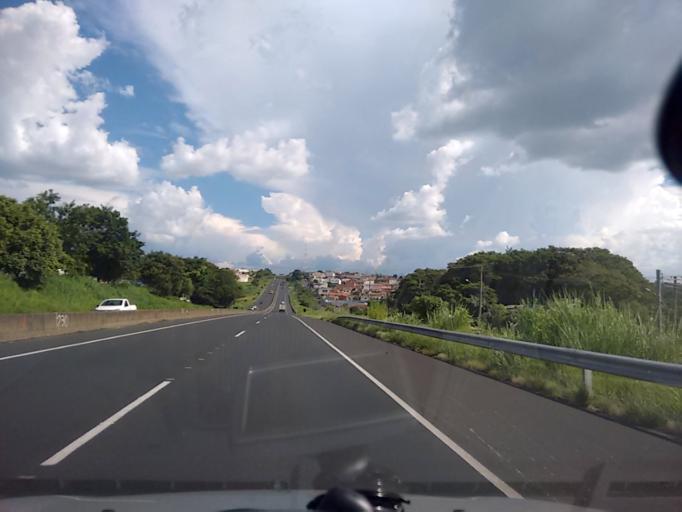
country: BR
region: Sao Paulo
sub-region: Marilia
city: Marilia
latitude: -22.1965
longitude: -49.9656
